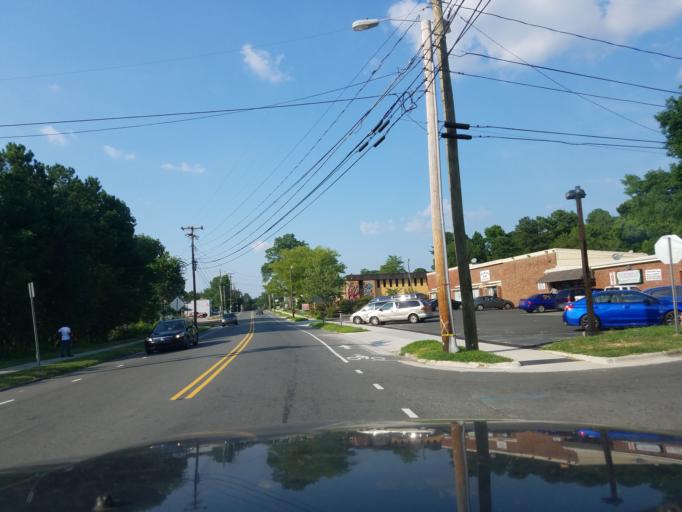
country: US
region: North Carolina
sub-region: Durham County
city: Durham
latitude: 35.9878
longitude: -78.9258
